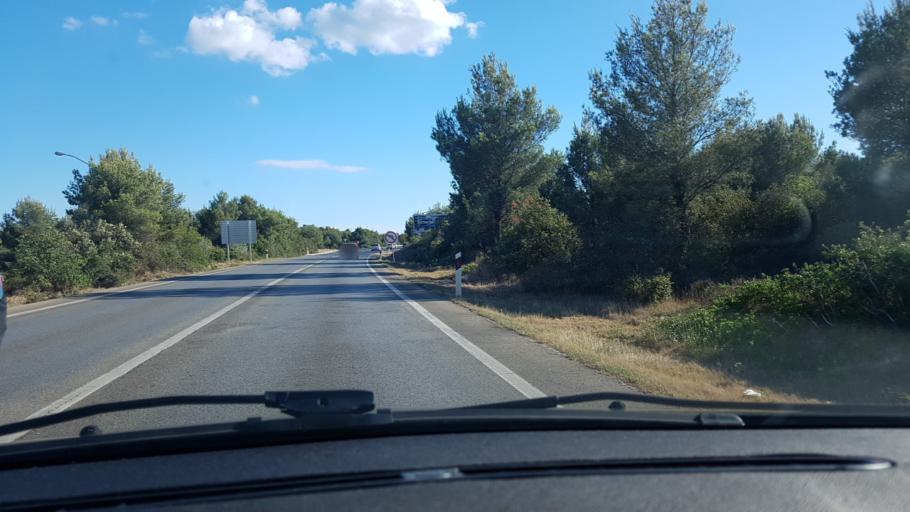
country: HR
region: Sibensko-Kniniska
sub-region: Grad Sibenik
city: Sibenik
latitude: 43.7021
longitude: 15.9069
